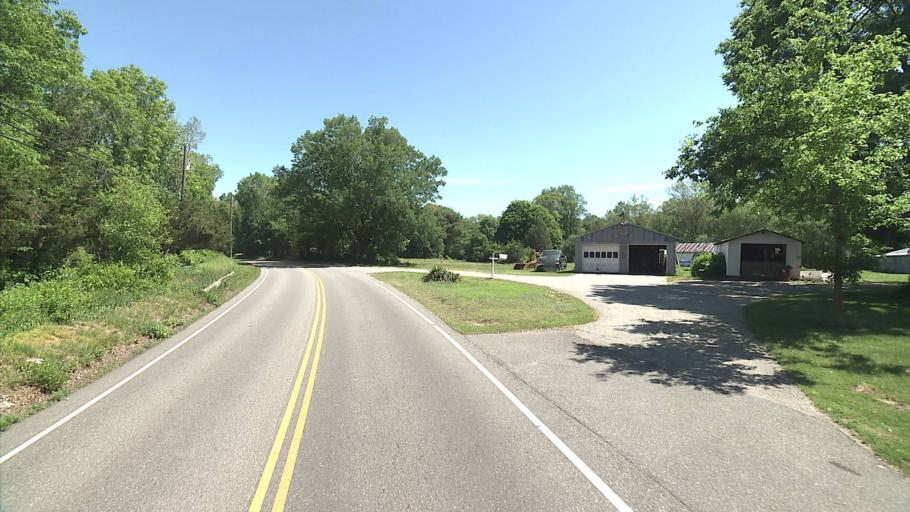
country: US
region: Rhode Island
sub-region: Washington County
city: Hopkinton
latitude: 41.4657
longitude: -71.8329
